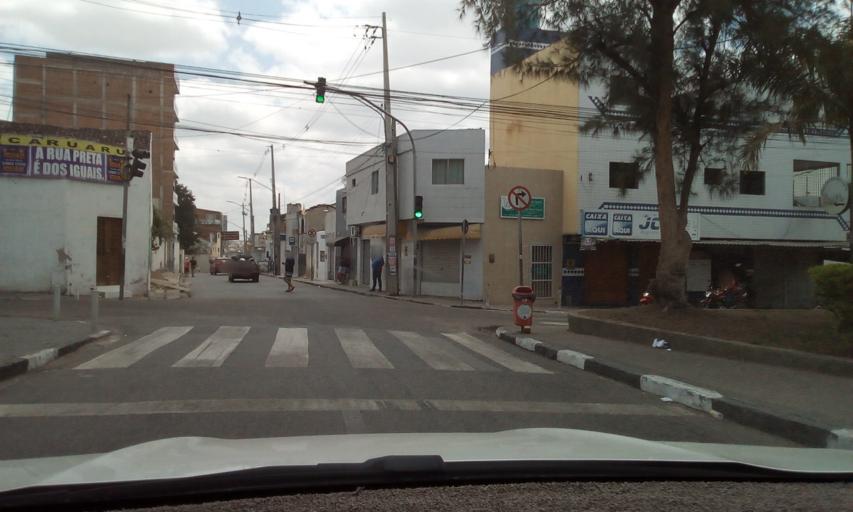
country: BR
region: Pernambuco
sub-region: Caruaru
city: Caruaru
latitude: -8.2890
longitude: -35.9789
